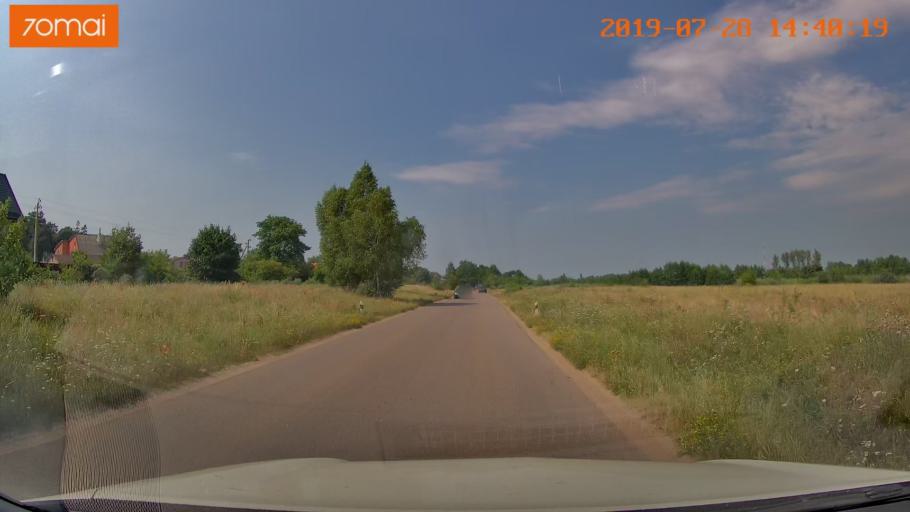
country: RU
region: Kaliningrad
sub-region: Gorod Kaliningrad
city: Yantarnyy
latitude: 54.8509
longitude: 19.9592
